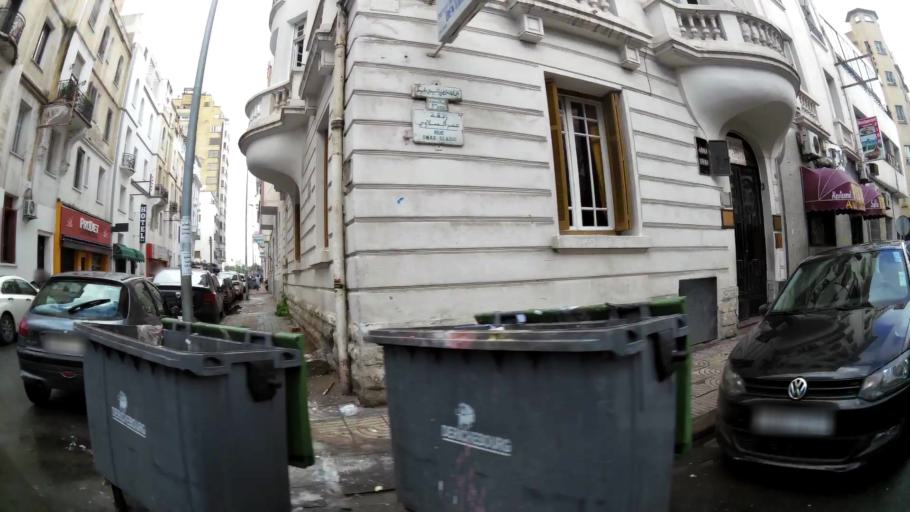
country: MA
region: Grand Casablanca
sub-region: Casablanca
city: Casablanca
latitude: 33.5884
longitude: -7.6190
